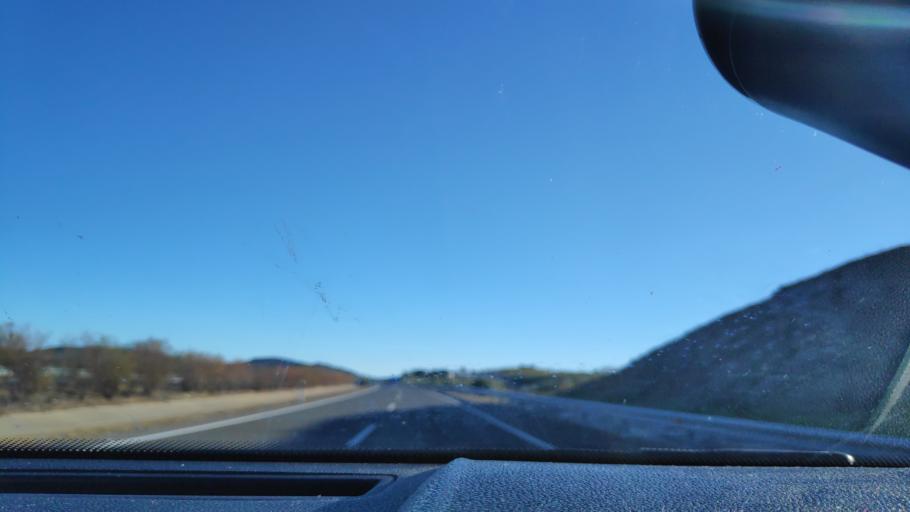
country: ES
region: Extremadura
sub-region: Provincia de Badajoz
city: Monesterio
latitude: 38.0994
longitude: -6.2694
